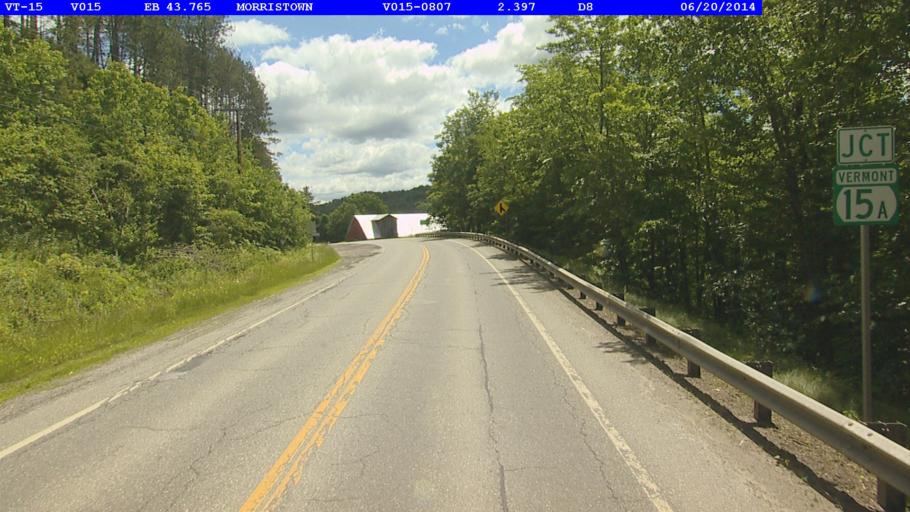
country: US
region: Vermont
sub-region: Lamoille County
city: Morrisville
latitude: 44.5664
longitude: -72.5666
